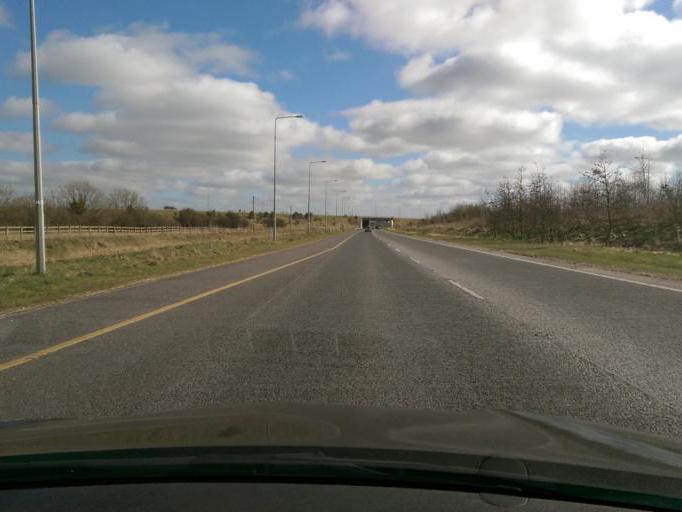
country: IE
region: Leinster
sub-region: An Iarmhi
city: Kinnegad
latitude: 53.4501
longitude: -7.1140
